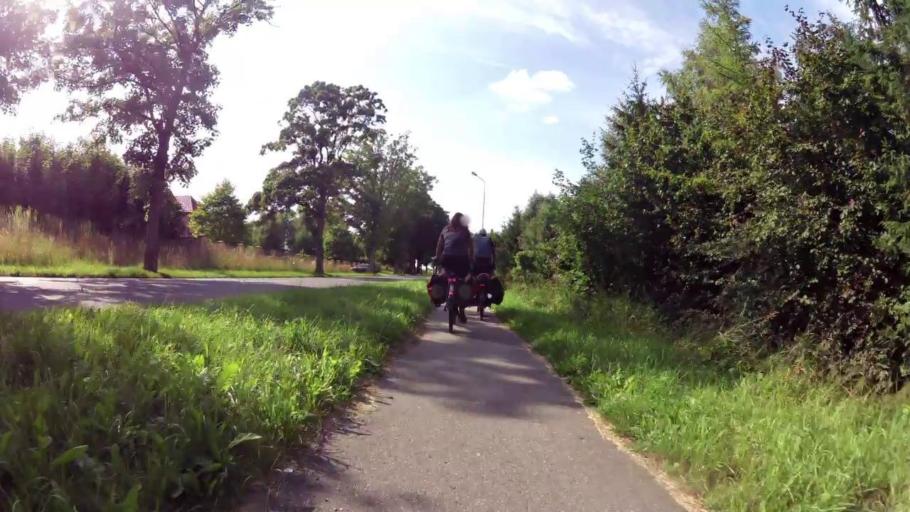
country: PL
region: West Pomeranian Voivodeship
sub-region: Powiat lobeski
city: Wegorzyno
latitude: 53.5479
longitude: 15.5469
